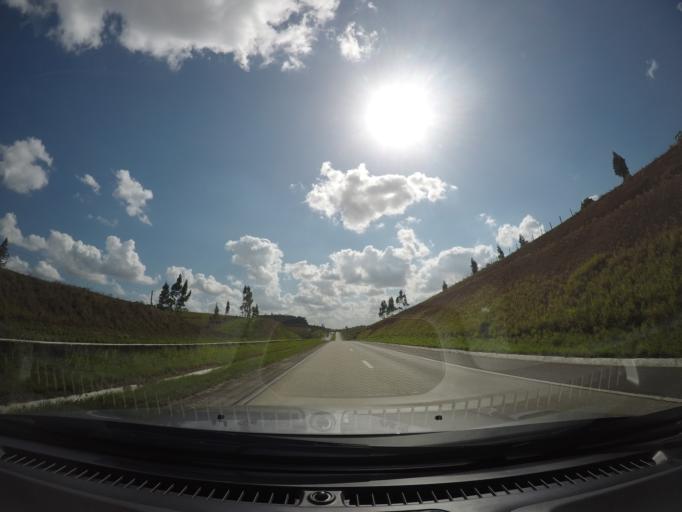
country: BR
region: Pernambuco
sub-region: Gameleira
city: Gameleira
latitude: -8.5582
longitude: -35.4643
